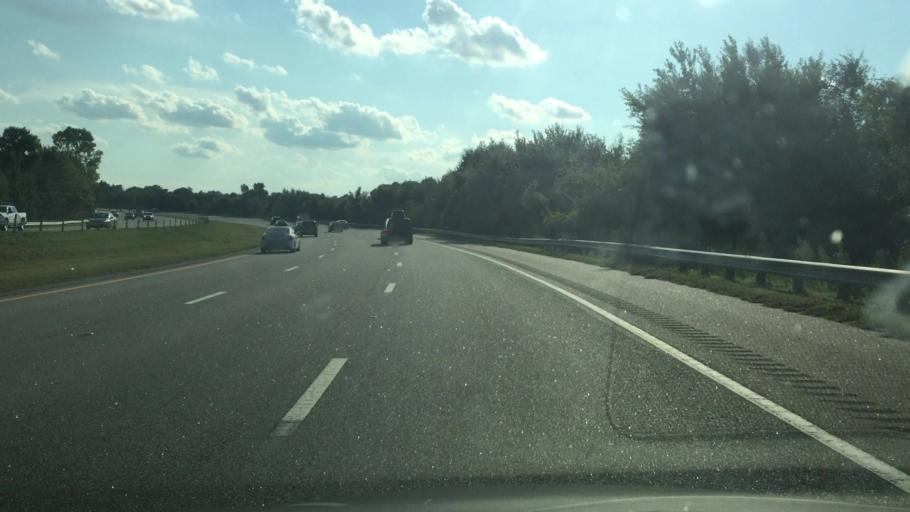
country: US
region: South Carolina
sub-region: Horry County
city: North Myrtle Beach
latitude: 33.8256
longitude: -78.7313
